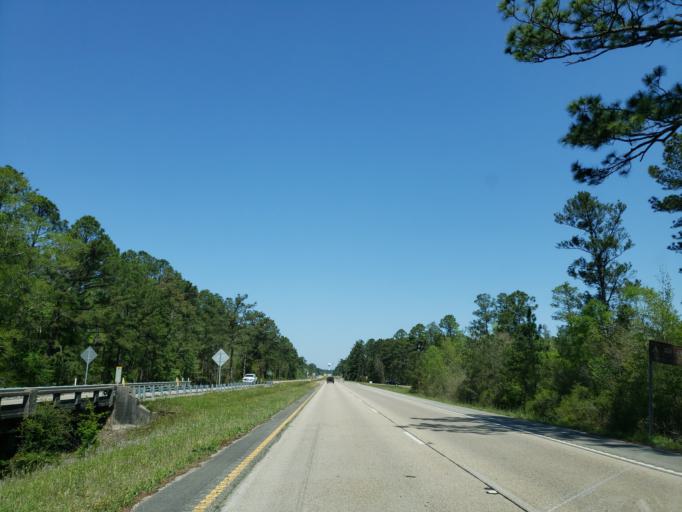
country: US
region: Mississippi
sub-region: Harrison County
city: Lyman
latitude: 30.5603
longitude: -89.1223
